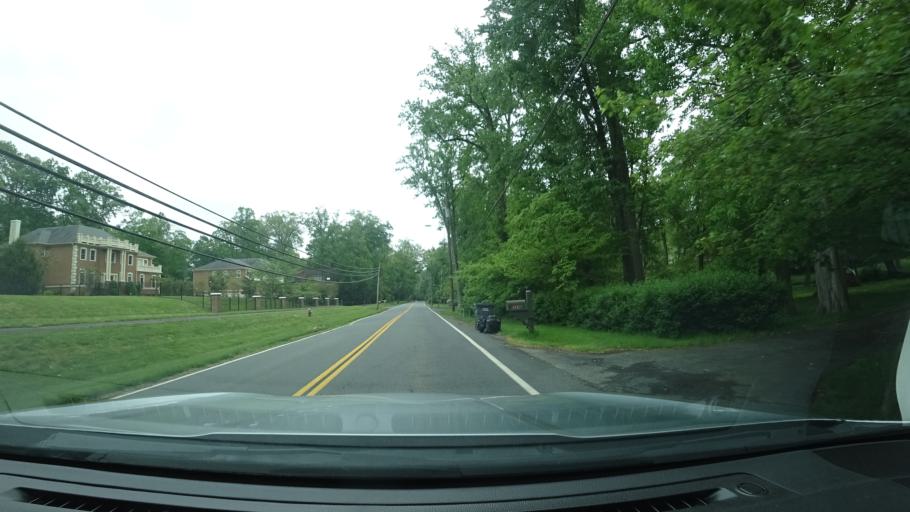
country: US
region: Virginia
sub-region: Fairfax County
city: Oakton
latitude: 38.8876
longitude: -77.3447
